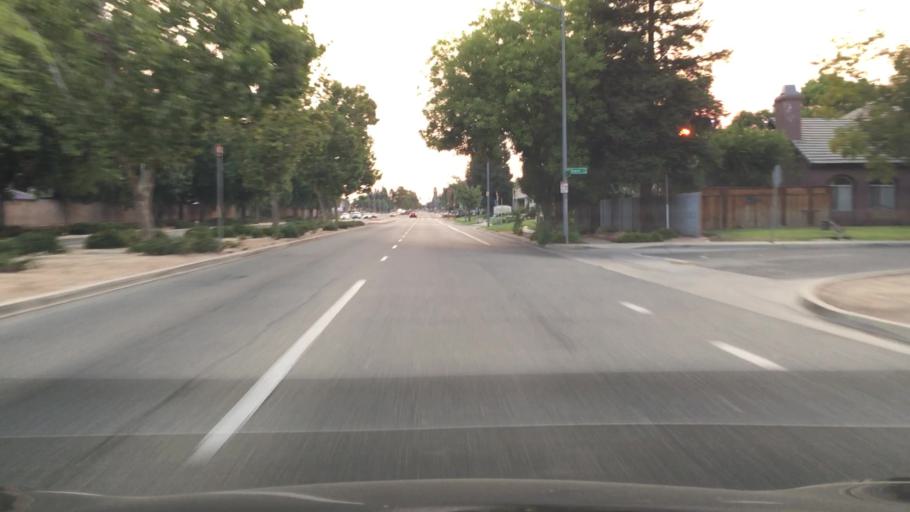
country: US
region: California
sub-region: Fresno County
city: Clovis
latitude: 36.8521
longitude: -119.7536
